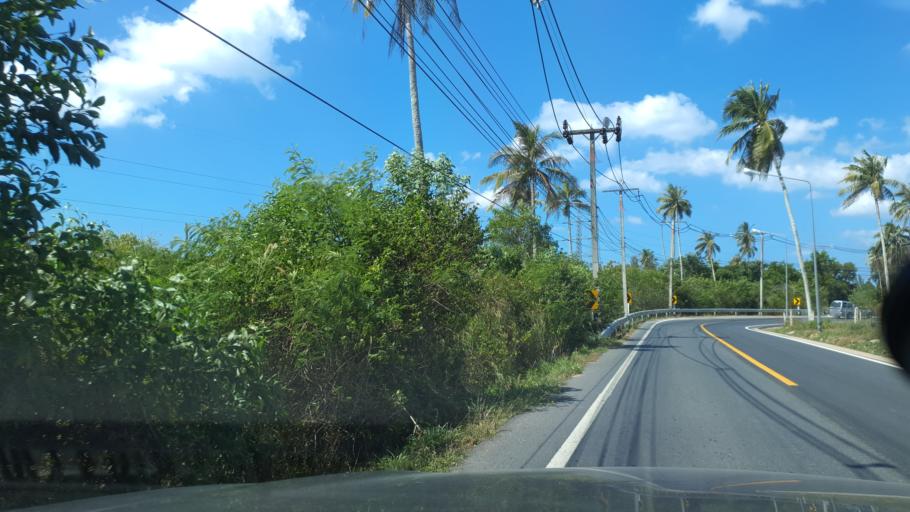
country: TH
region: Phuket
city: Thalang
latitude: 8.1563
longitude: 98.3038
